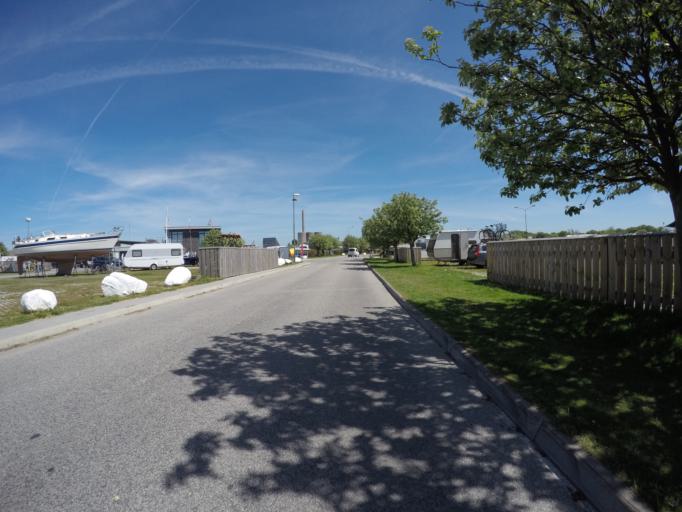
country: SE
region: Skane
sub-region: Malmo
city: Bunkeflostrand
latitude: 55.5842
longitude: 12.9193
